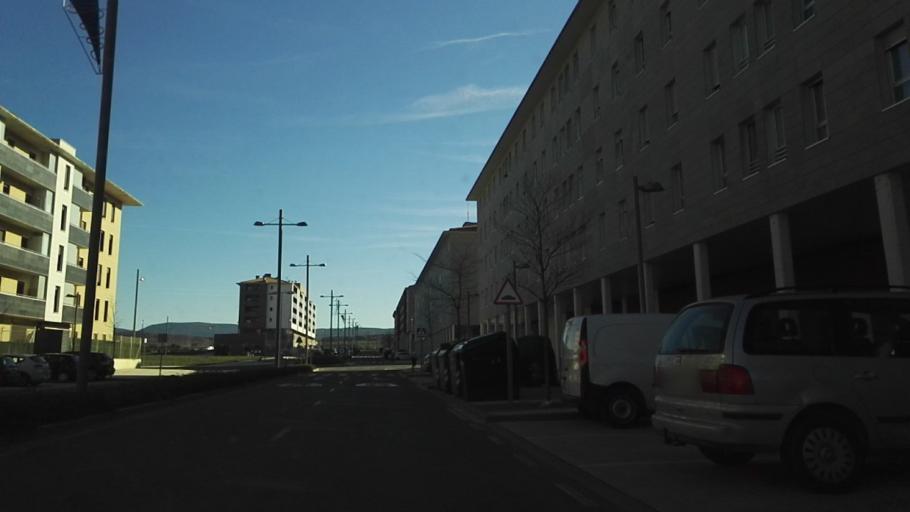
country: ES
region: Navarre
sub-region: Provincia de Navarra
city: Burlata
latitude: 42.7951
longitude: -1.6170
